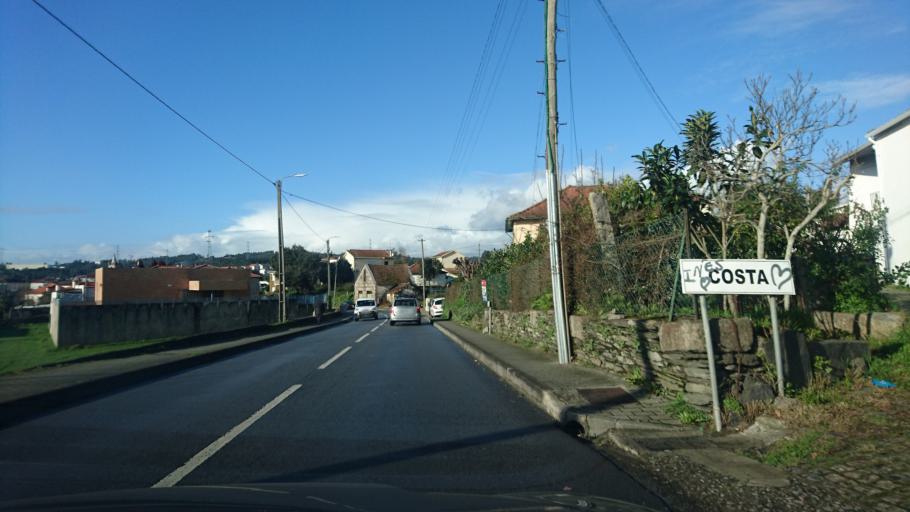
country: PT
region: Porto
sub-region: Paredes
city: Recarei
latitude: 41.1527
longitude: -8.4088
